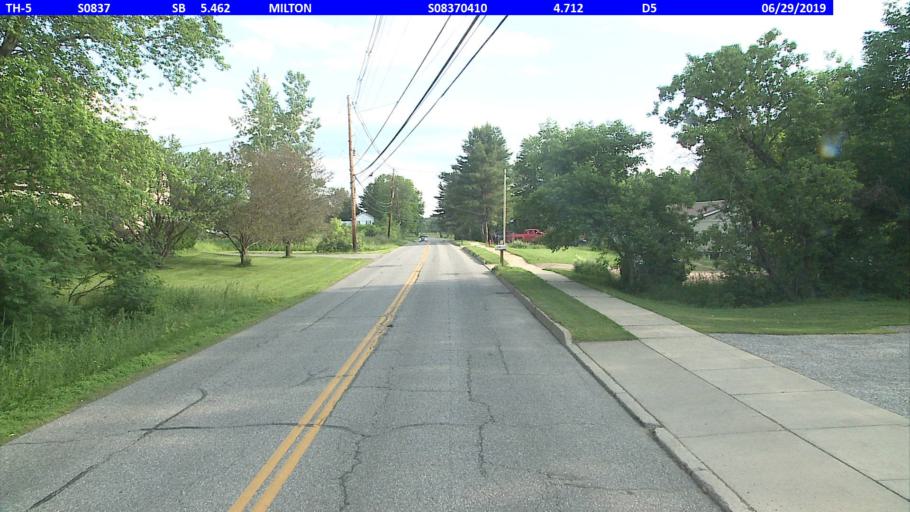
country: US
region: Vermont
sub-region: Chittenden County
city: Milton
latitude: 44.6408
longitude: -73.1006
